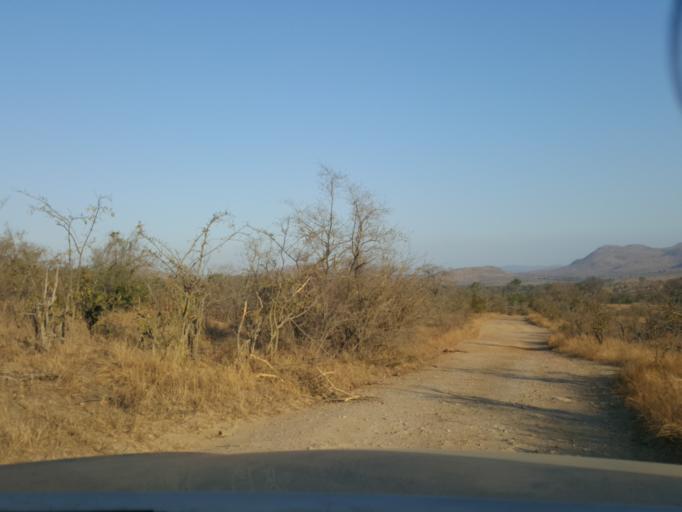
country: SZ
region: Hhohho
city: Ntfonjeni
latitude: -25.4079
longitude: 31.4396
